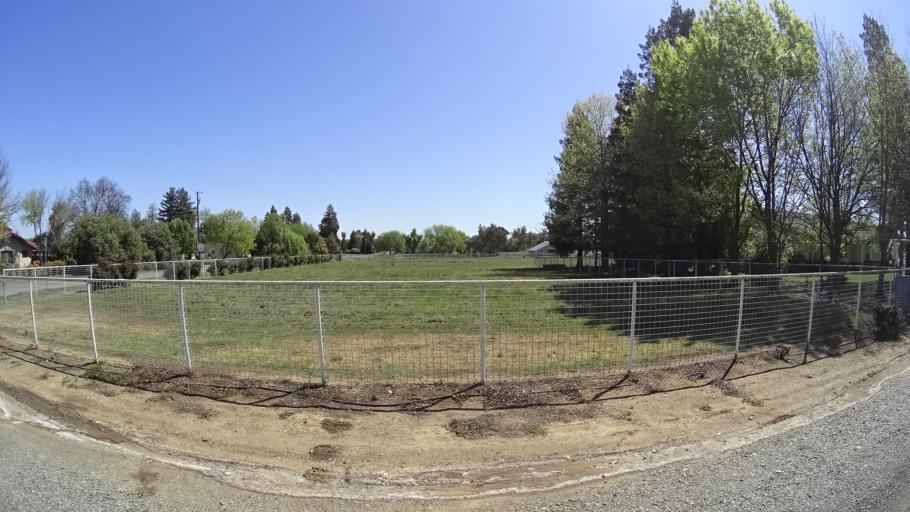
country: US
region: California
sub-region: Glenn County
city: Willows
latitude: 39.5331
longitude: -122.2121
